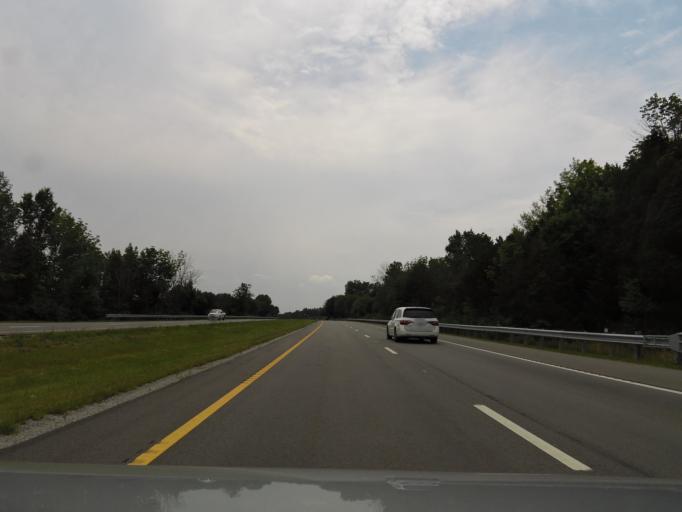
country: US
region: Ohio
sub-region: Warren County
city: Waynesville
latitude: 39.5479
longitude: -84.0539
